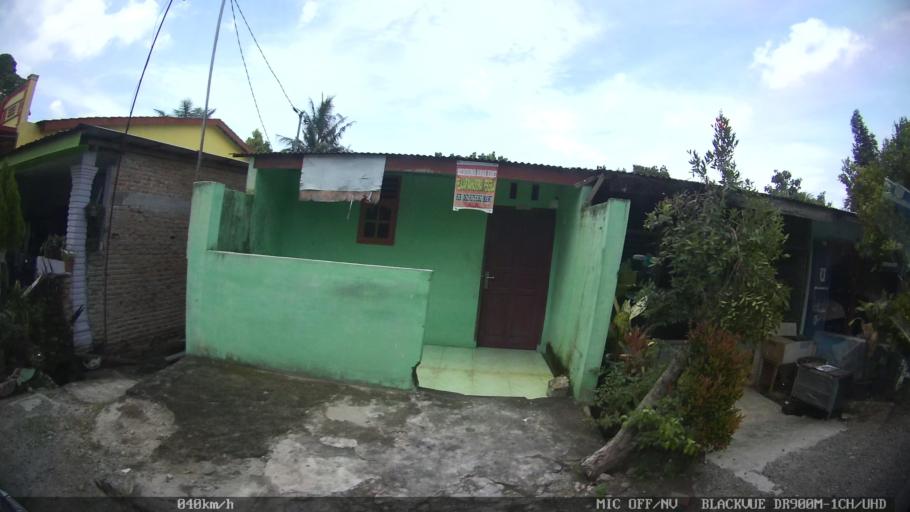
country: ID
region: North Sumatra
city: Percut
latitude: 3.5525
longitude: 98.8713
